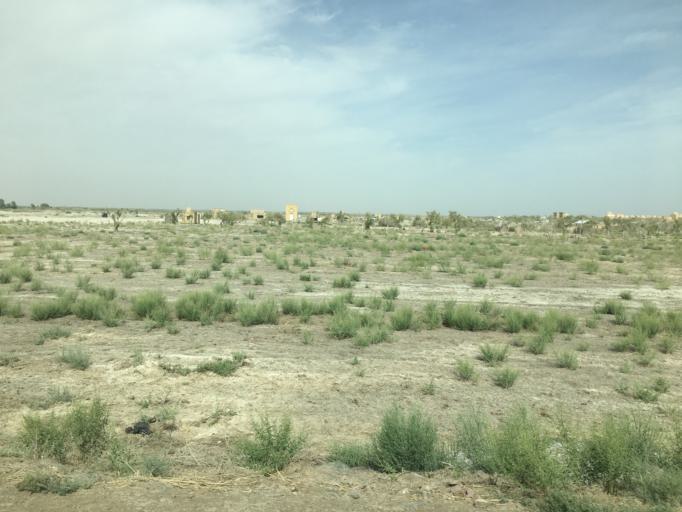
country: TM
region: Dasoguz
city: Tagta
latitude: 41.5653
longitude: 59.8156
